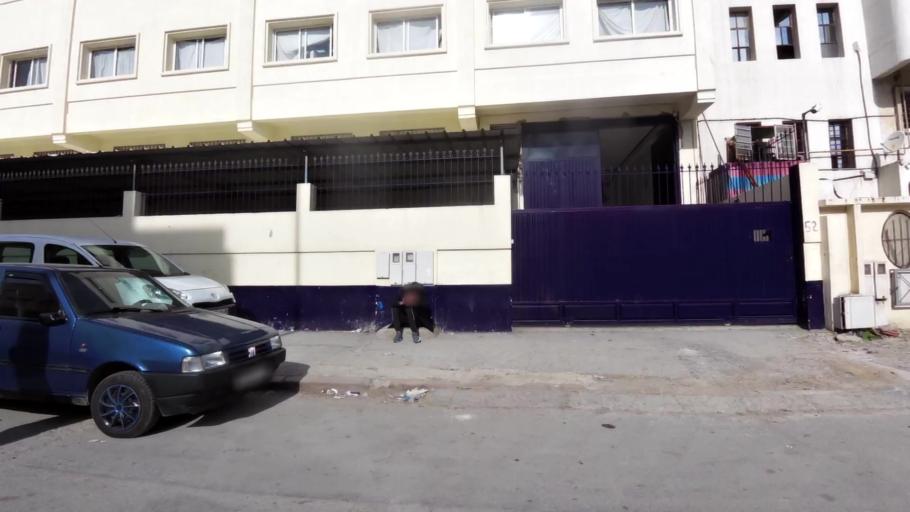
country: MA
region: Tanger-Tetouan
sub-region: Tanger-Assilah
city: Tangier
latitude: 35.7416
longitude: -5.7951
